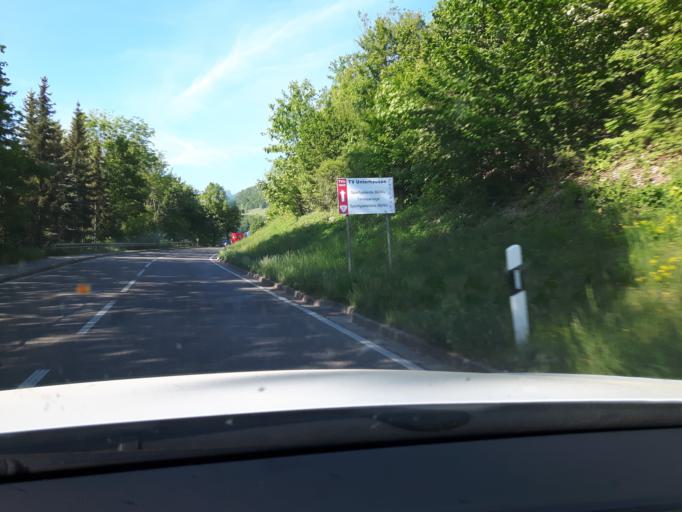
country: DE
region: Baden-Wuerttemberg
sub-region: Tuebingen Region
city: Pfullingen
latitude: 48.4361
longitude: 9.2608
